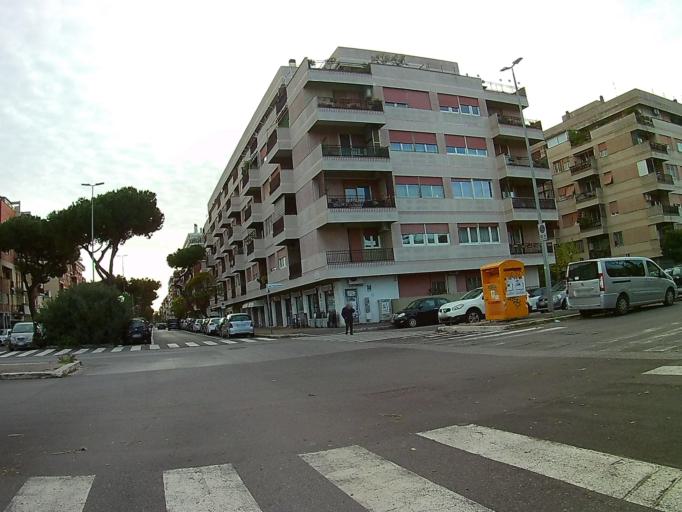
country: IT
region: Latium
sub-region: Citta metropolitana di Roma Capitale
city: Lido di Ostia
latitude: 41.7393
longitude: 12.2870
